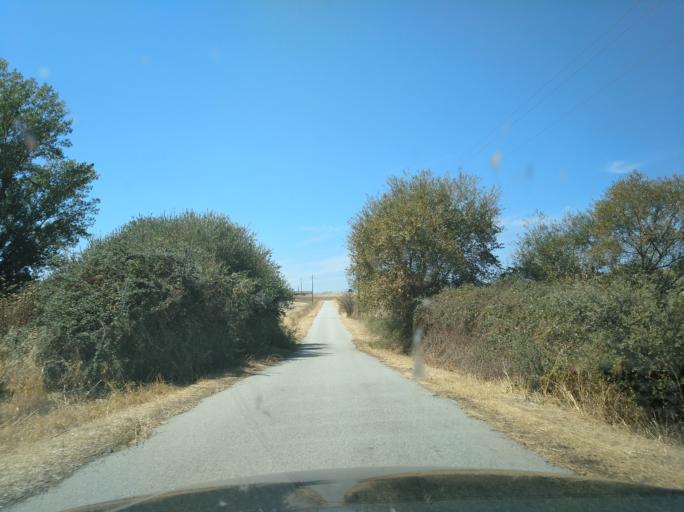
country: PT
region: Portalegre
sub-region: Campo Maior
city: Campo Maior
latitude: 38.9616
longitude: -7.1095
